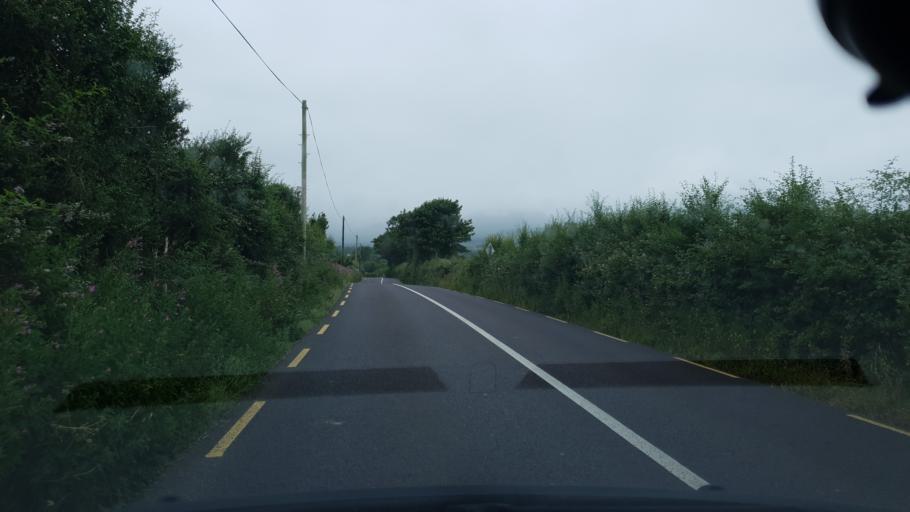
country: IE
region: Munster
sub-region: Ciarrai
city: Tralee
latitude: 52.1623
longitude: -9.6927
